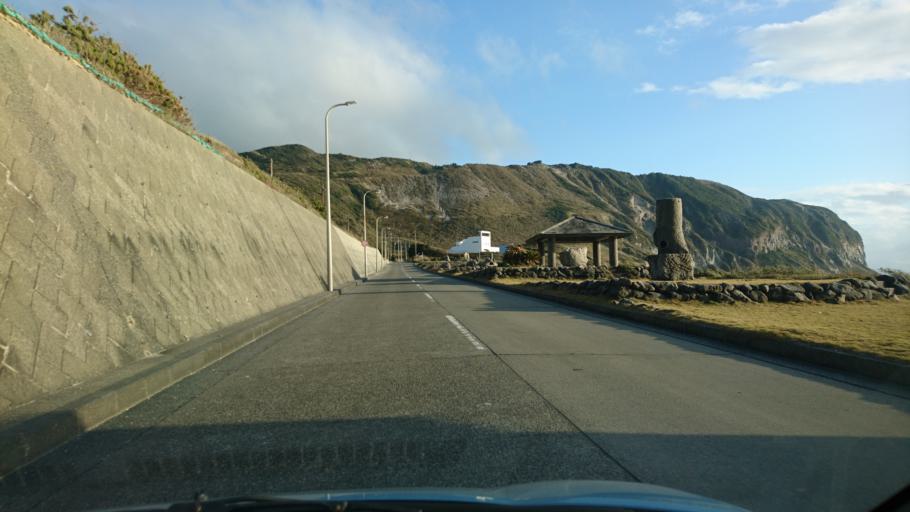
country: JP
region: Shizuoka
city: Shimoda
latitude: 34.3626
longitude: 139.2438
